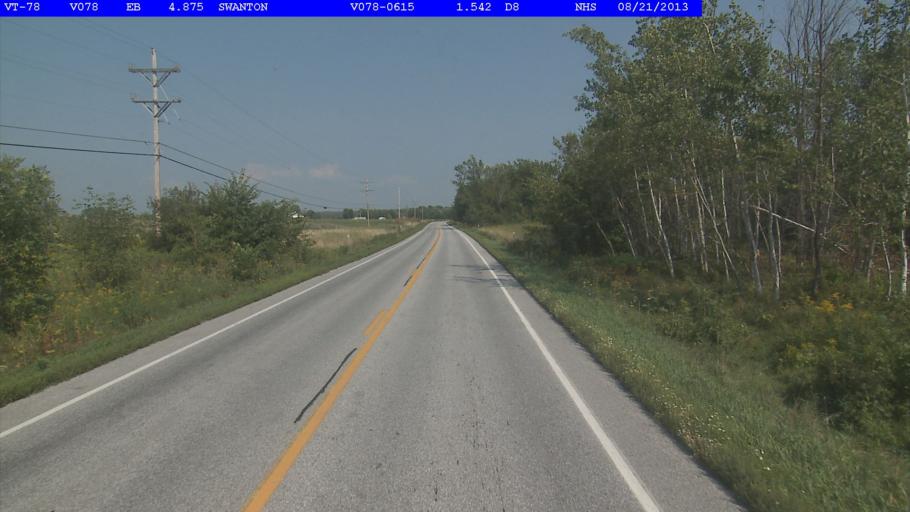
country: US
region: Vermont
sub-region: Franklin County
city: Swanton
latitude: 44.9703
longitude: -73.1898
